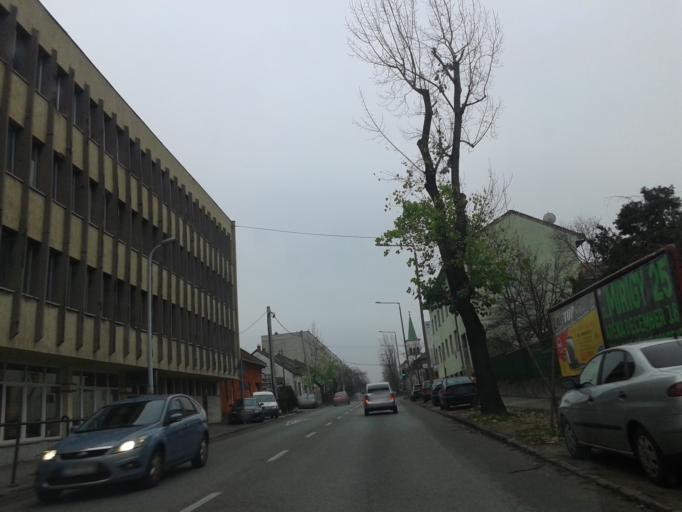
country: HU
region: Budapest
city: Budapest XXI. keruelet
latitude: 47.4327
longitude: 19.0727
